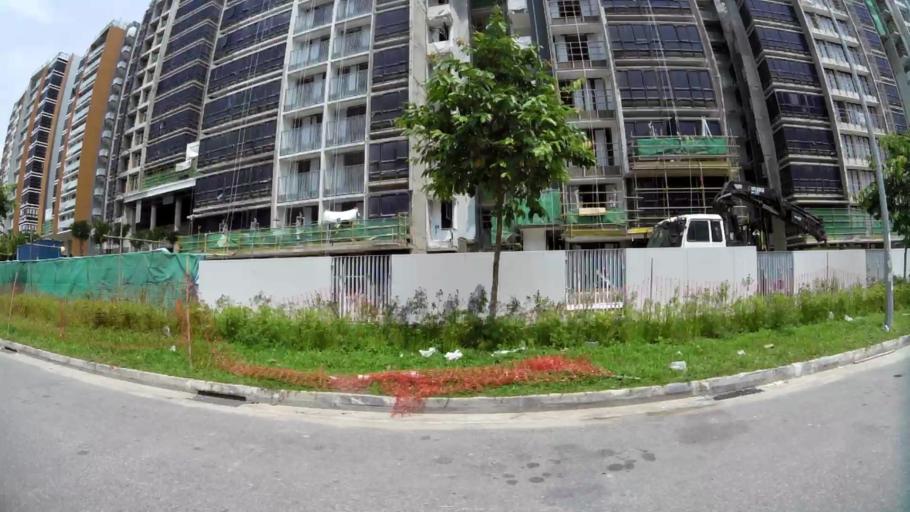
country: MY
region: Johor
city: Kampung Pasir Gudang Baru
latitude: 1.3708
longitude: 103.9462
